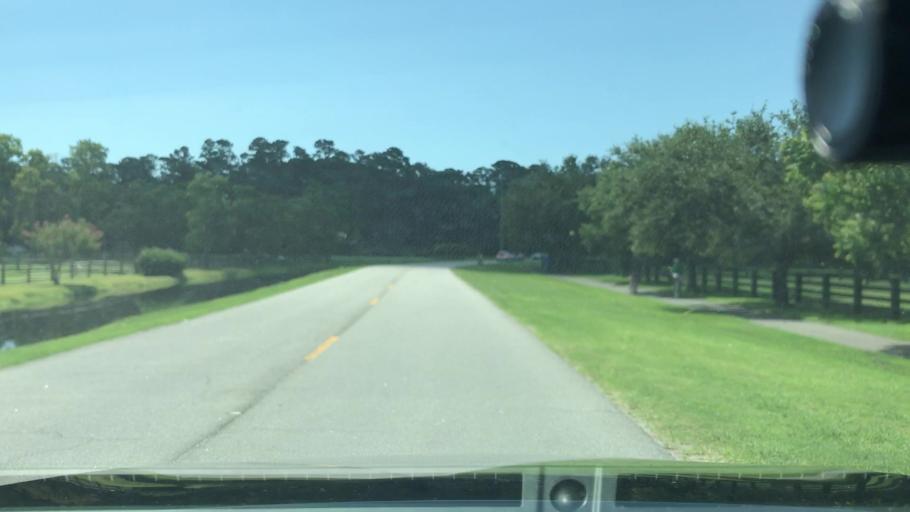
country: US
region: South Carolina
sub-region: Beaufort County
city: Hilton Head Island
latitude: 32.1416
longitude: -80.7888
